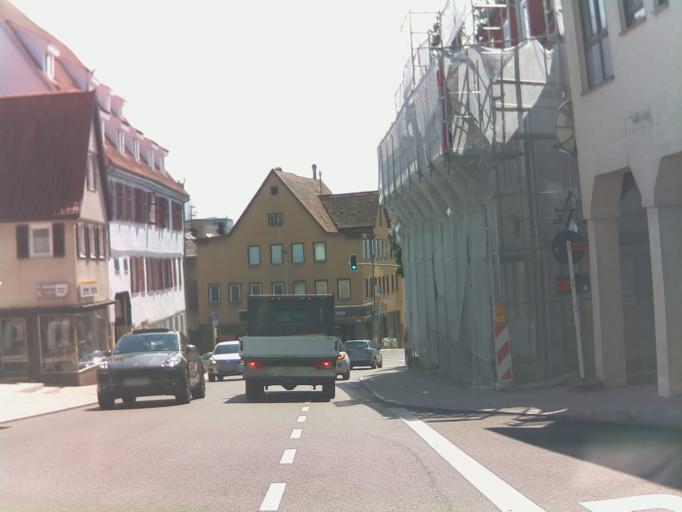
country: DE
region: Baden-Wuerttemberg
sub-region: Regierungsbezirk Stuttgart
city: Leonberg
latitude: 48.8013
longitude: 9.0166
